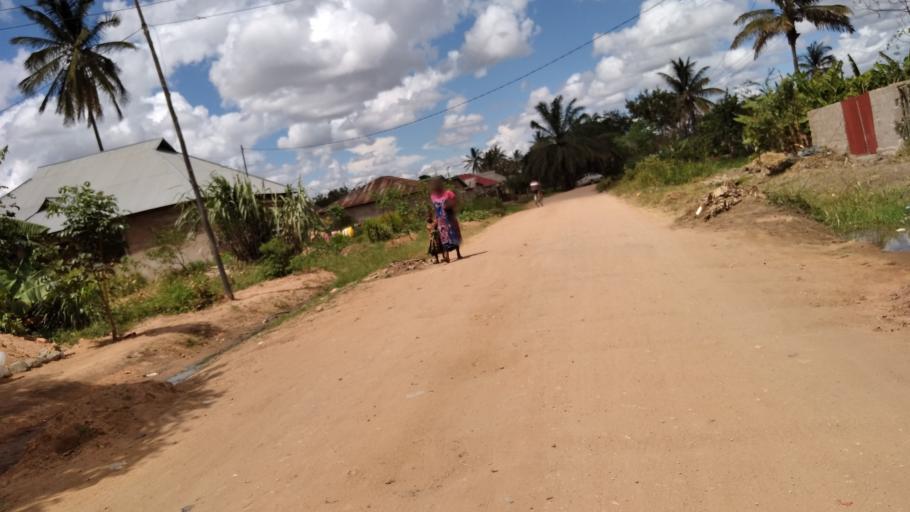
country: TZ
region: Dodoma
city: Dodoma
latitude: -6.1670
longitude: 35.7381
